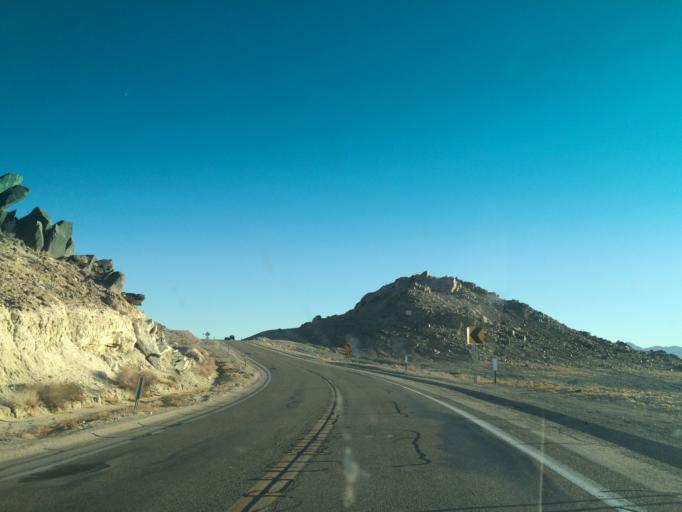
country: US
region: California
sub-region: San Bernardino County
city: Searles Valley
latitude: 35.6848
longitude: -117.3845
